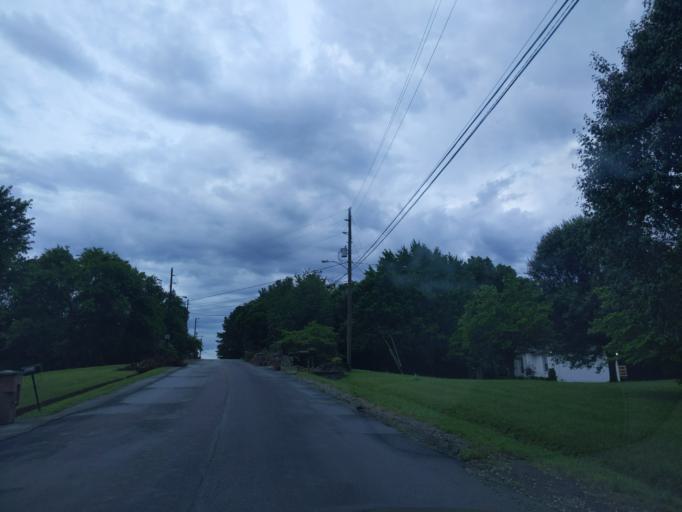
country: US
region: Tennessee
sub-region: Williamson County
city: Brentwood Estates
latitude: 36.0384
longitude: -86.7401
